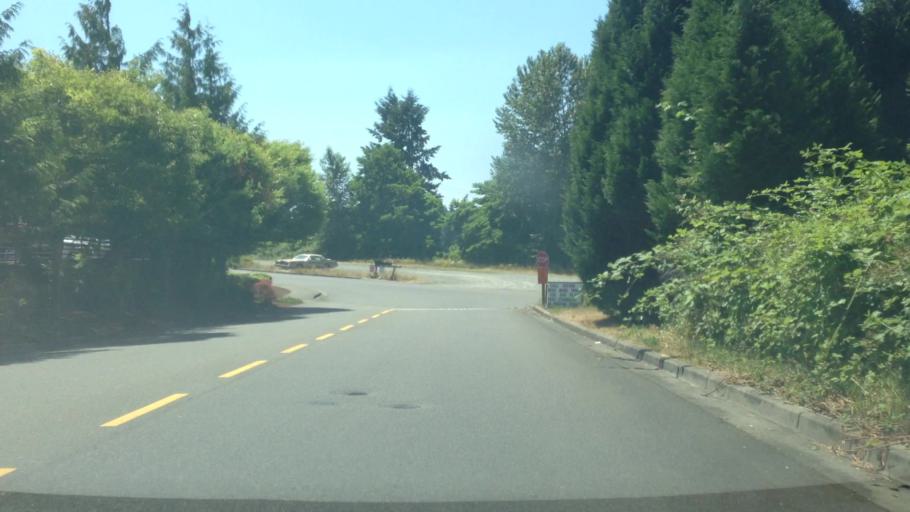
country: US
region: Washington
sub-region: Pierce County
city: Puyallup
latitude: 47.1565
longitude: -122.3095
